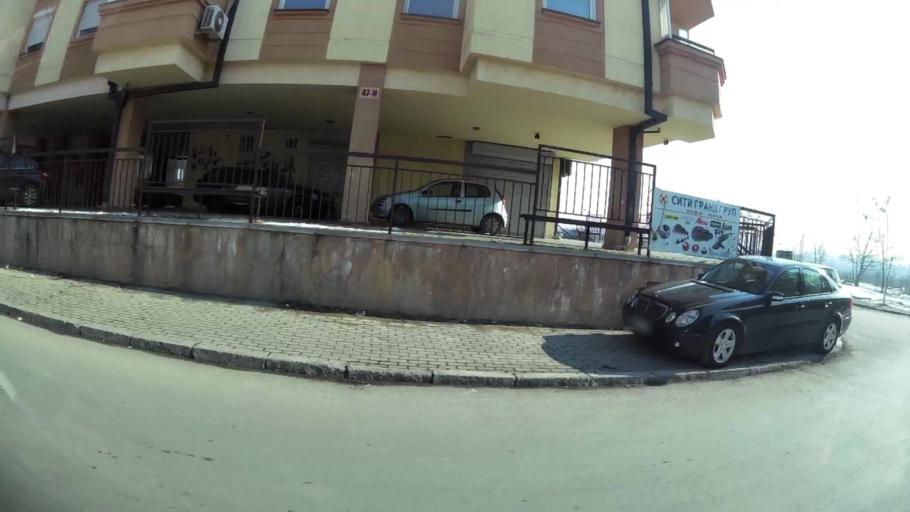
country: MK
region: Kisela Voda
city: Usje
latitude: 41.9762
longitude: 21.4463
